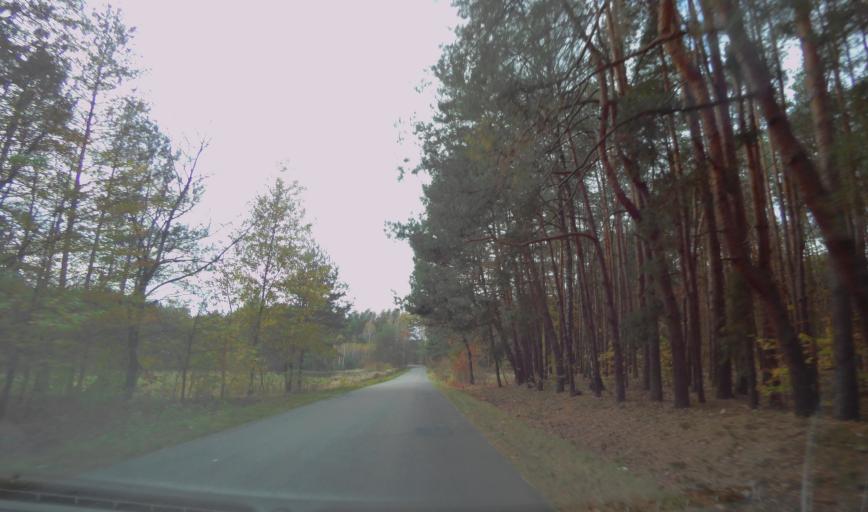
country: PL
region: Subcarpathian Voivodeship
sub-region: Powiat lezajski
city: Wola Zarczycka
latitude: 50.2659
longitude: 22.2479
